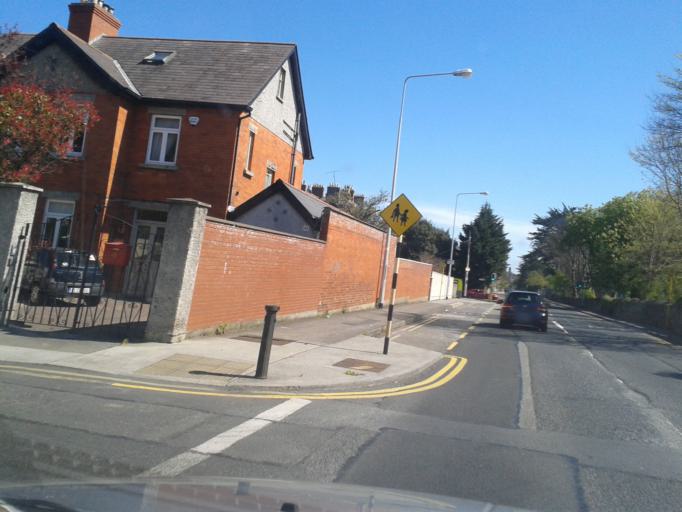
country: IE
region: Leinster
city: Blackrock
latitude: 53.2955
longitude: -6.1666
